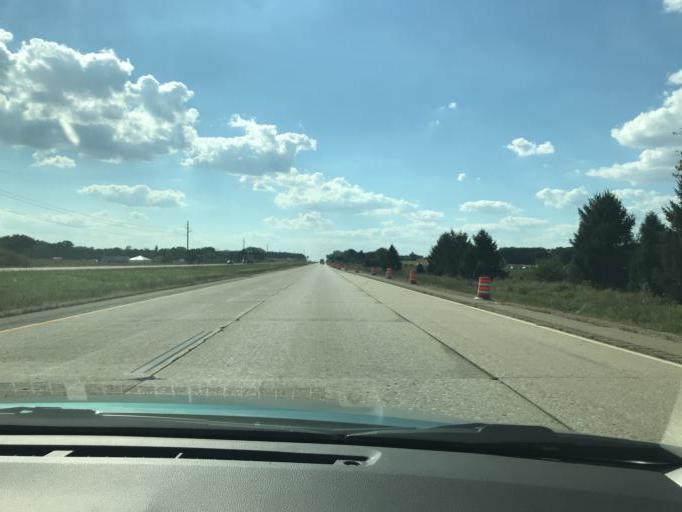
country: US
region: Wisconsin
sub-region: Walworth County
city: Darien
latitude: 42.6203
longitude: -88.6796
